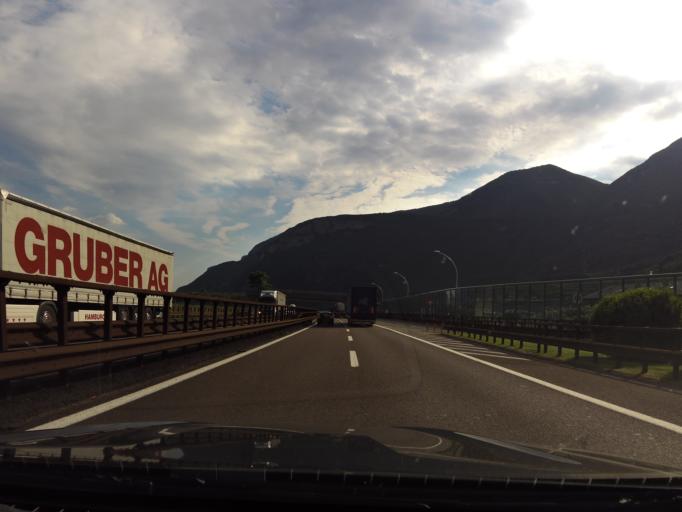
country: IT
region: Veneto
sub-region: Provincia di Verona
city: Rivalta
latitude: 45.6918
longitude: 10.9111
